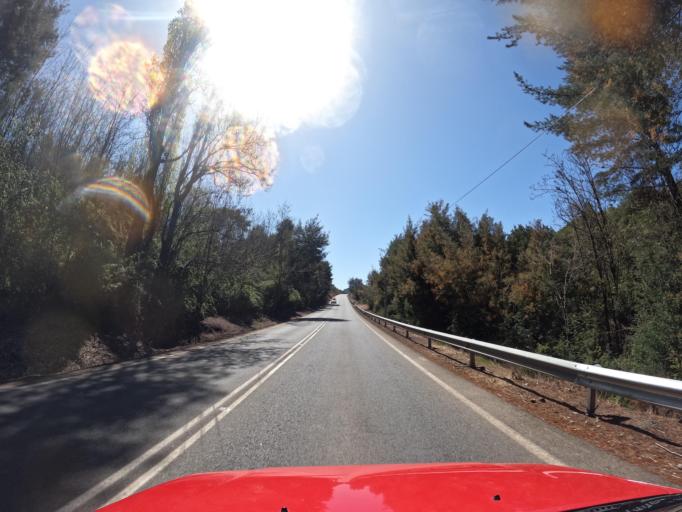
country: CL
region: Maule
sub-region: Provincia de Talca
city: San Clemente
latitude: -35.4541
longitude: -71.2694
